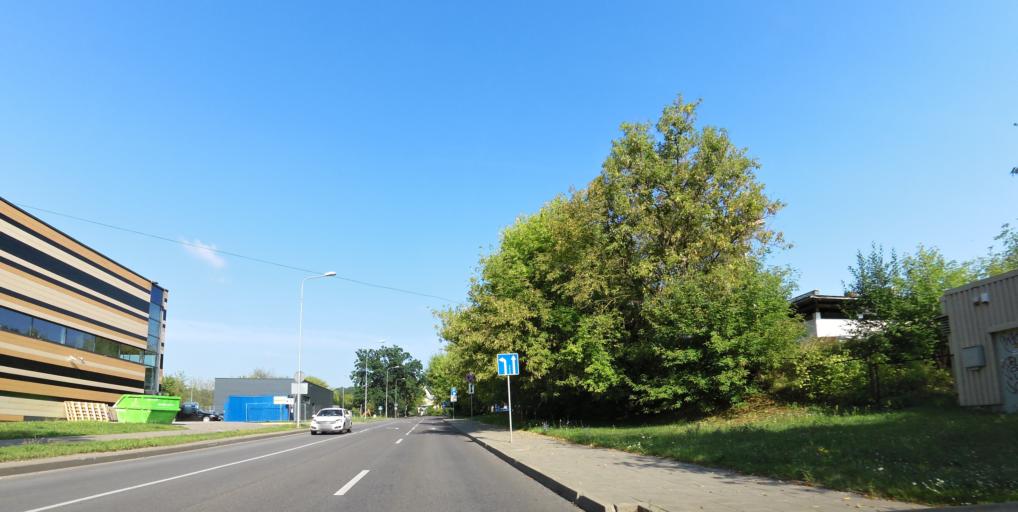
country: LT
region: Vilnius County
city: Seskine
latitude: 54.7013
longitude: 25.2581
